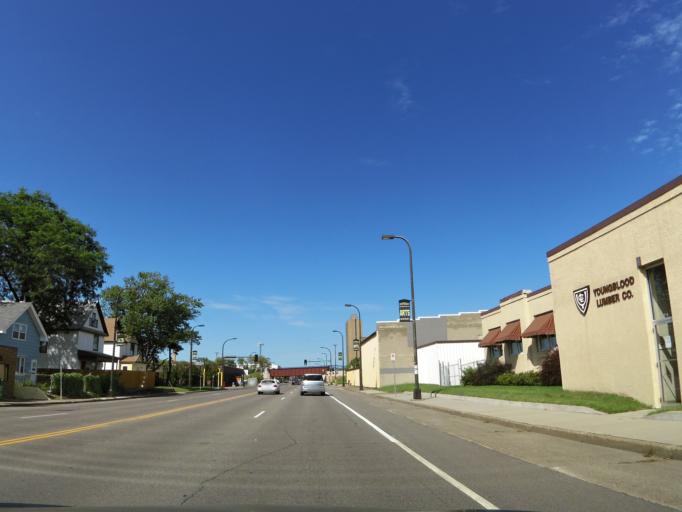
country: US
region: Minnesota
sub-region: Hennepin County
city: Minneapolis
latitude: 45.0010
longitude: -93.2473
